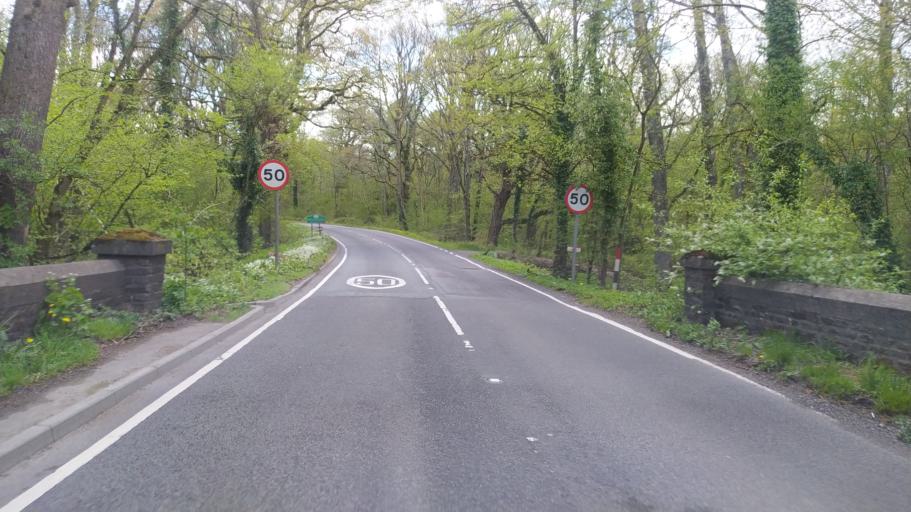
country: GB
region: England
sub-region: Wiltshire
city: Kilmington
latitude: 51.1742
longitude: -2.3008
